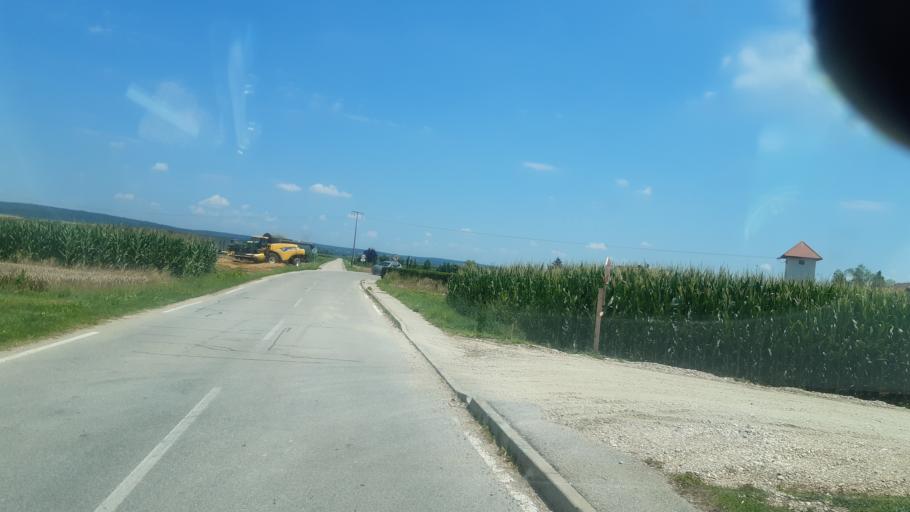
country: SI
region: Moravske Toplice
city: Moravske Toplice
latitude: 46.6704
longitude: 16.2159
